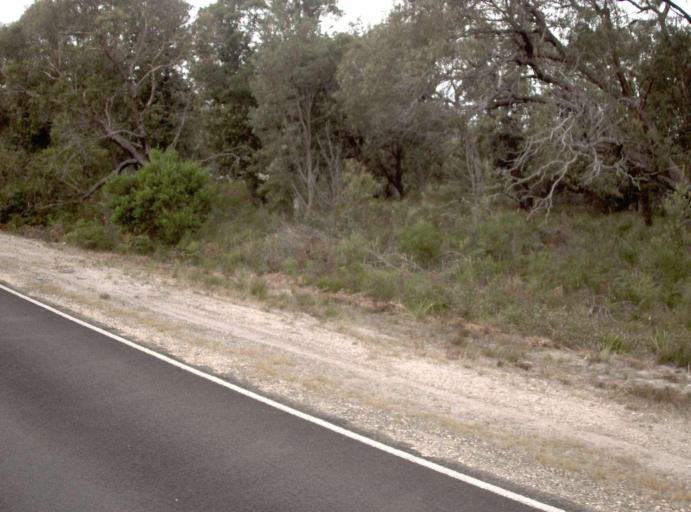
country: AU
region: Victoria
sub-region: East Gippsland
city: Bairnsdale
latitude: -38.0690
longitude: 147.5511
